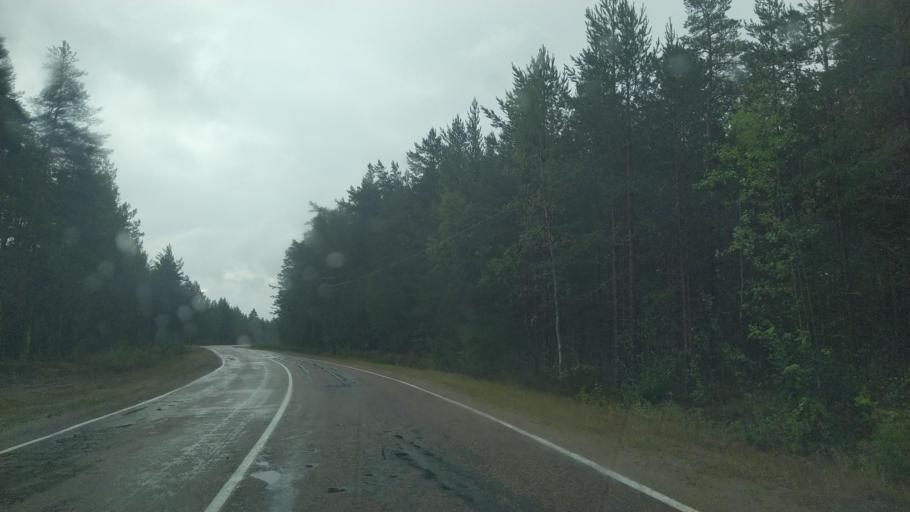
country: RU
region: Leningrad
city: Priozersk
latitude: 60.9794
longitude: 30.2711
